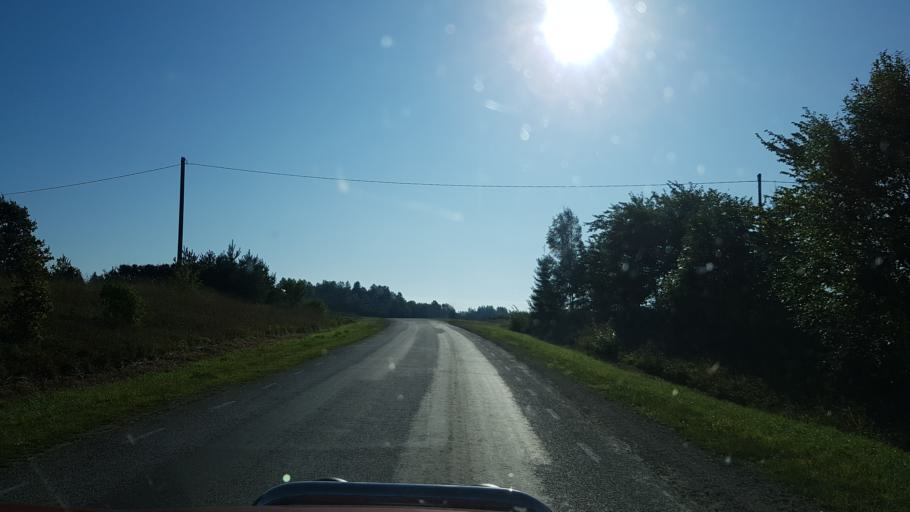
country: EE
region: Jogevamaa
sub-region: Tabivere vald
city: Tabivere
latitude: 58.6792
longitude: 26.6251
